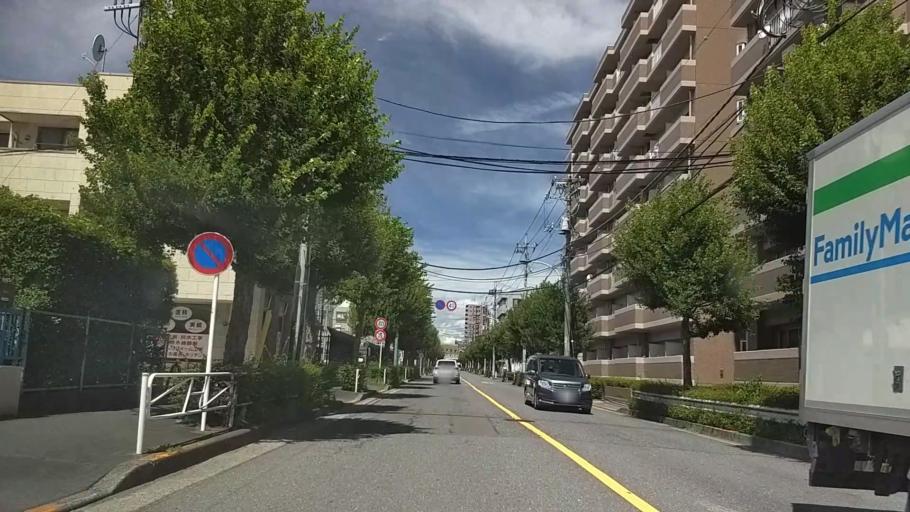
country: JP
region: Tokyo
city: Hachioji
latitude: 35.6563
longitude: 139.3496
